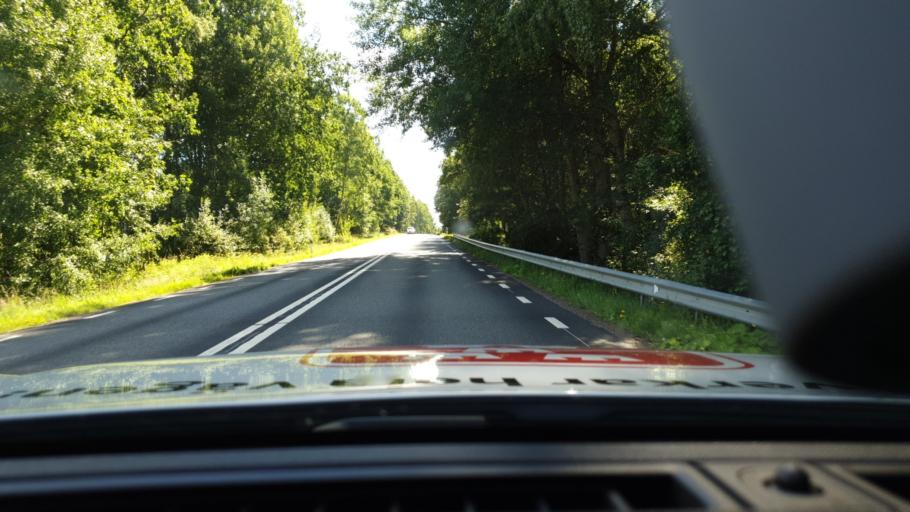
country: SE
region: Joenkoeping
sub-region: Jonkopings Kommun
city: Graenna
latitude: 58.0124
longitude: 14.5282
